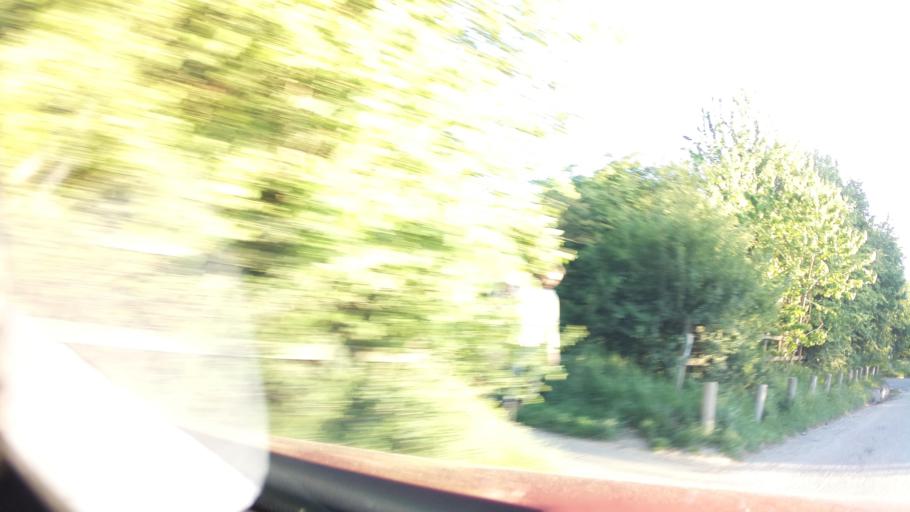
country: GB
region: England
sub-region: Devon
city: Newton Abbot
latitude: 50.5495
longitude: -3.6124
